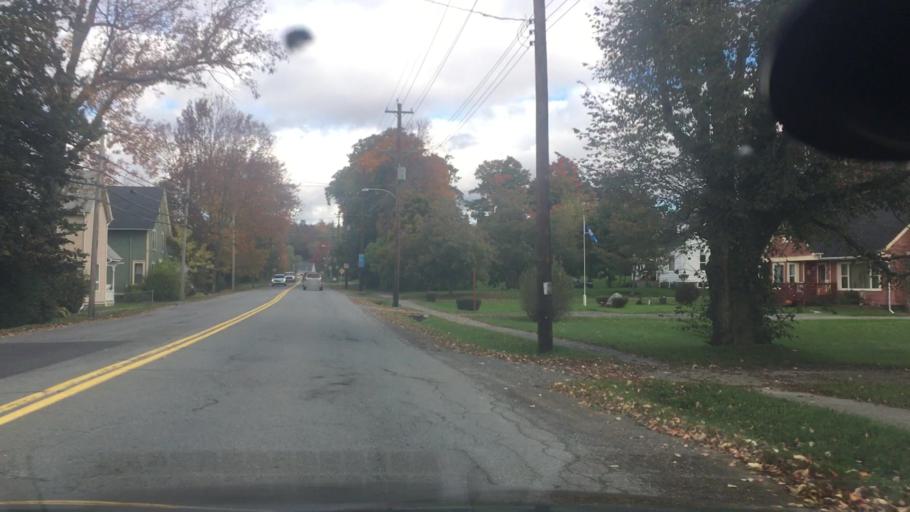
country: CA
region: Nova Scotia
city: Windsor
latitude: 44.9822
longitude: -64.1302
